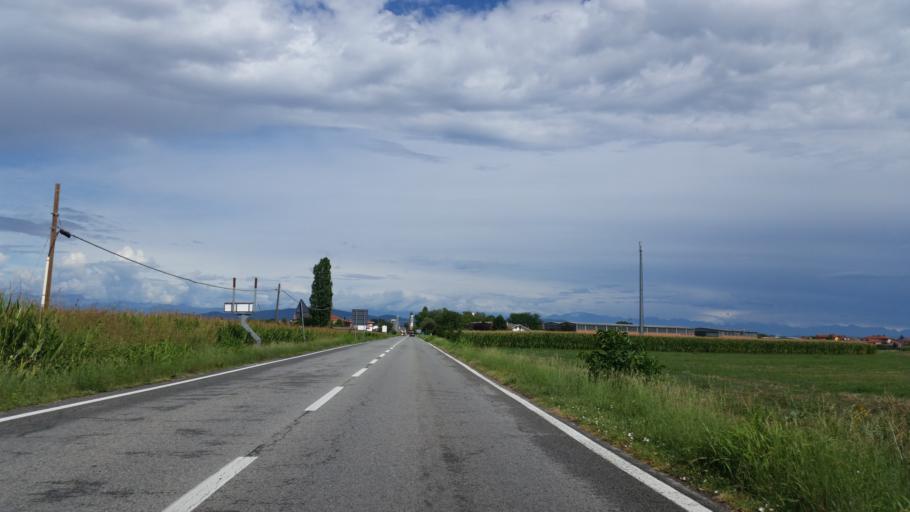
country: IT
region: Piedmont
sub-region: Provincia di Torino
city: Poirino
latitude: 44.9079
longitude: 7.8535
